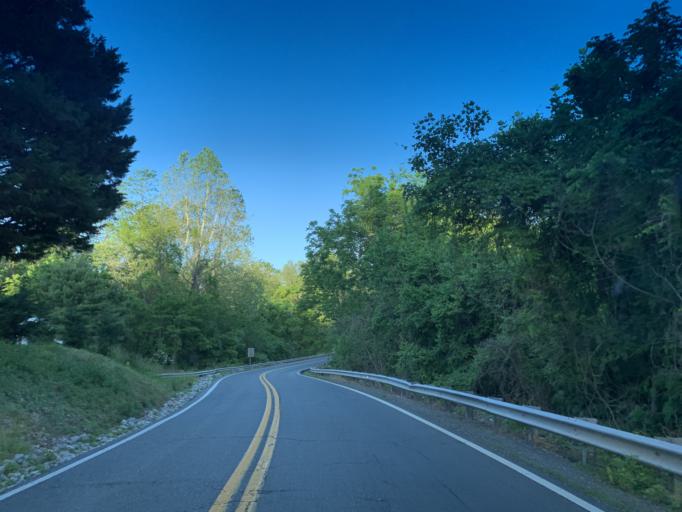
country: US
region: Maryland
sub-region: Cecil County
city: Elkton
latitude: 39.6576
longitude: -75.8236
